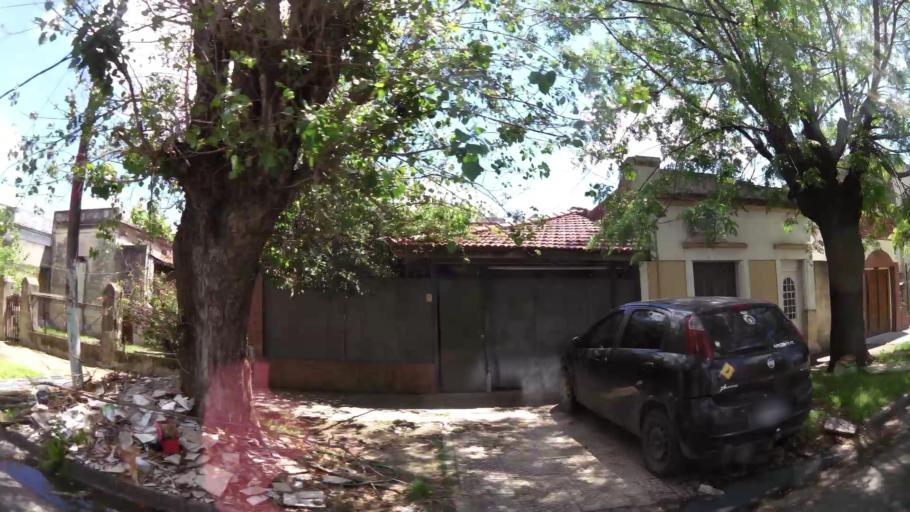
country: AR
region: Buenos Aires
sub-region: Partido de Lomas de Zamora
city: Lomas de Zamora
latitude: -34.7325
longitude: -58.4042
